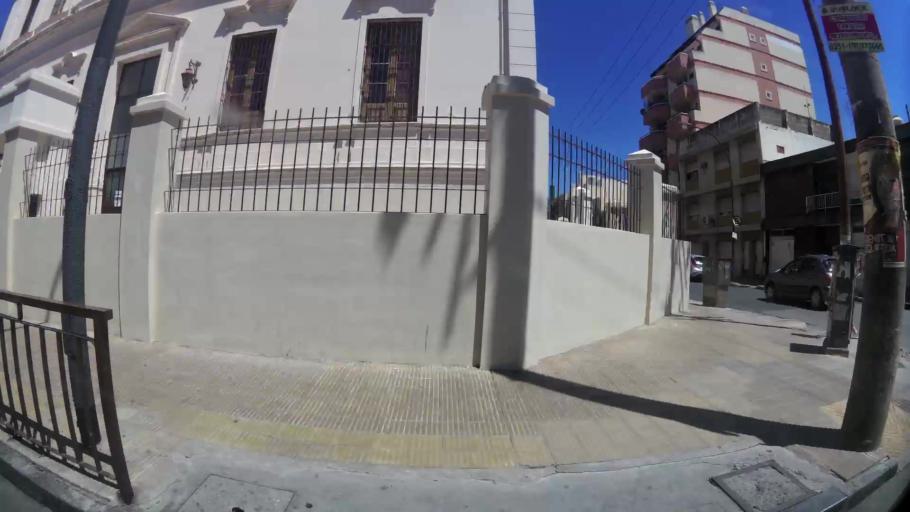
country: AR
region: Cordoba
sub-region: Departamento de Capital
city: Cordoba
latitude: -31.4132
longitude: -64.1980
